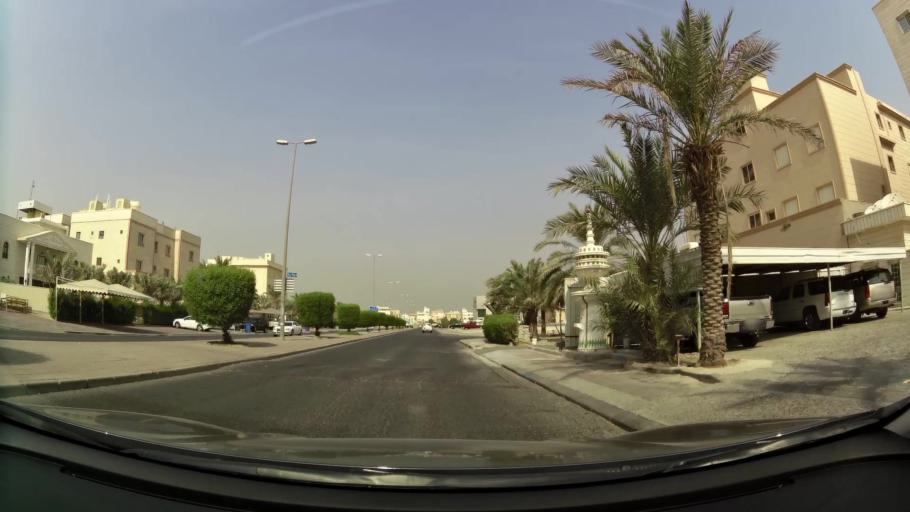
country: KW
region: Al Asimah
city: Ar Rabiyah
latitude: 29.3068
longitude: 47.8735
